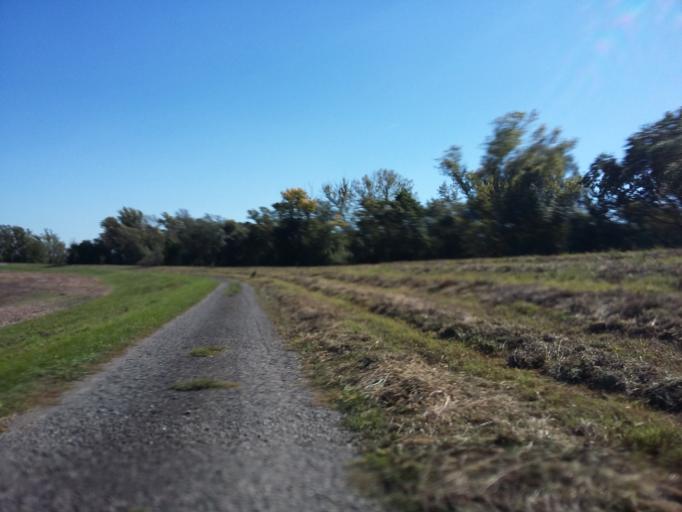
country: AT
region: Lower Austria
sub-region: Politischer Bezirk Ganserndorf
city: Marchegg
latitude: 48.2997
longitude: 16.9225
